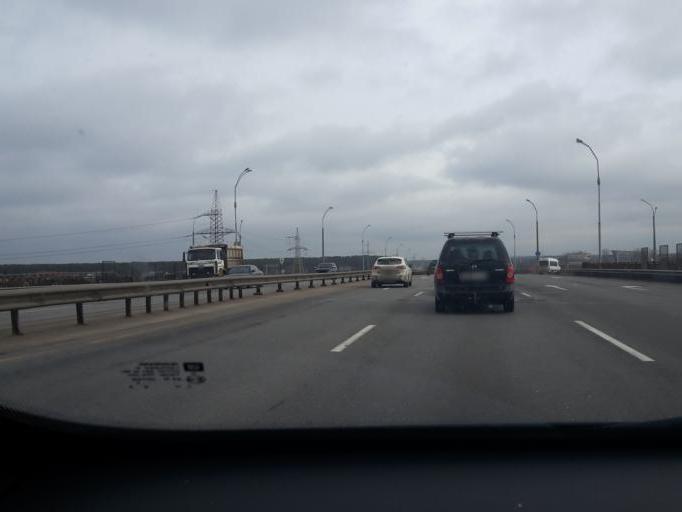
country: BY
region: Minsk
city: Zhdanovichy
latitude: 53.9423
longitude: 27.4345
